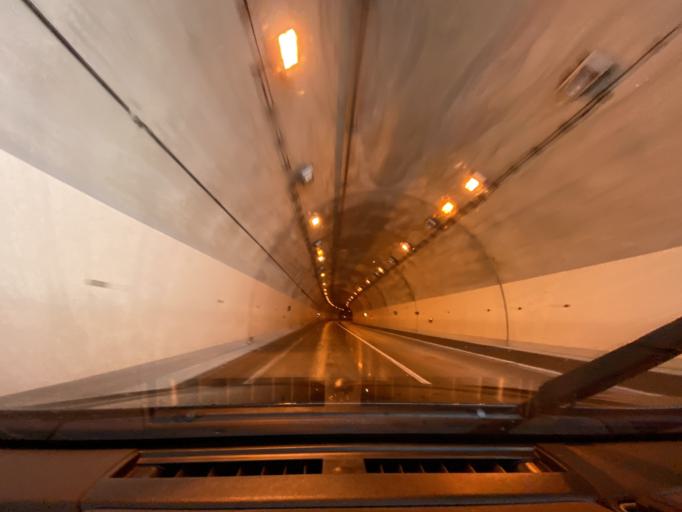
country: JP
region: Hokkaido
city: Rumoi
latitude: 43.8134
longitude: 141.4116
